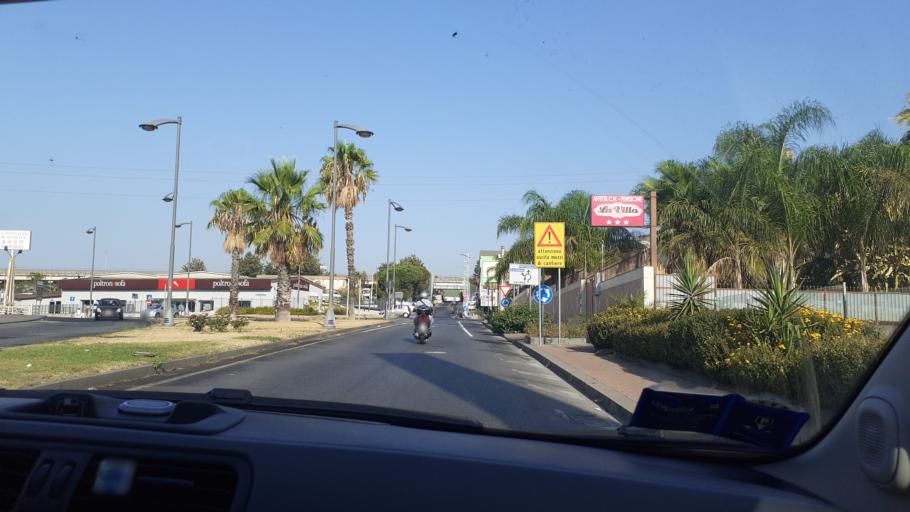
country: IT
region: Sicily
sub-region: Catania
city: Misterbianco
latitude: 37.5150
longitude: 15.0232
